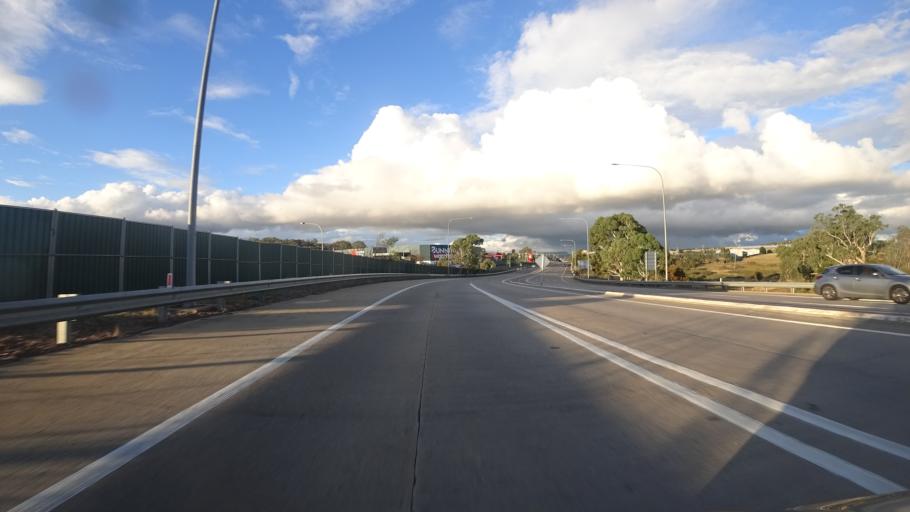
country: AU
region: New South Wales
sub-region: Goulburn Mulwaree
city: Goulburn
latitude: -34.7750
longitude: 149.6875
